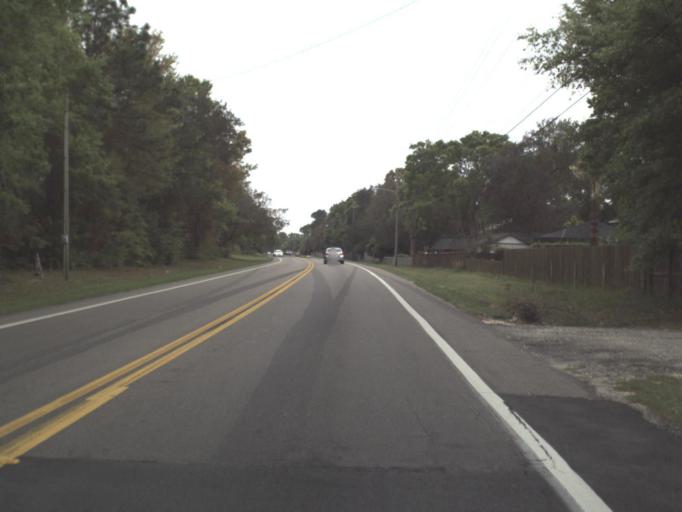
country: US
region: Florida
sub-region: Escambia County
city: East Pensacola Heights
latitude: 30.4455
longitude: -87.1734
